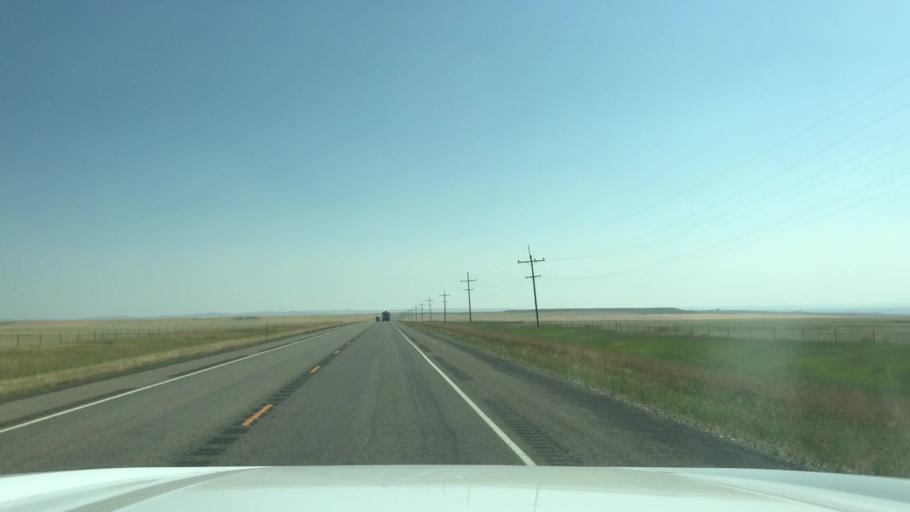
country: US
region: Montana
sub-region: Wheatland County
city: Harlowton
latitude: 46.5039
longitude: -109.7661
